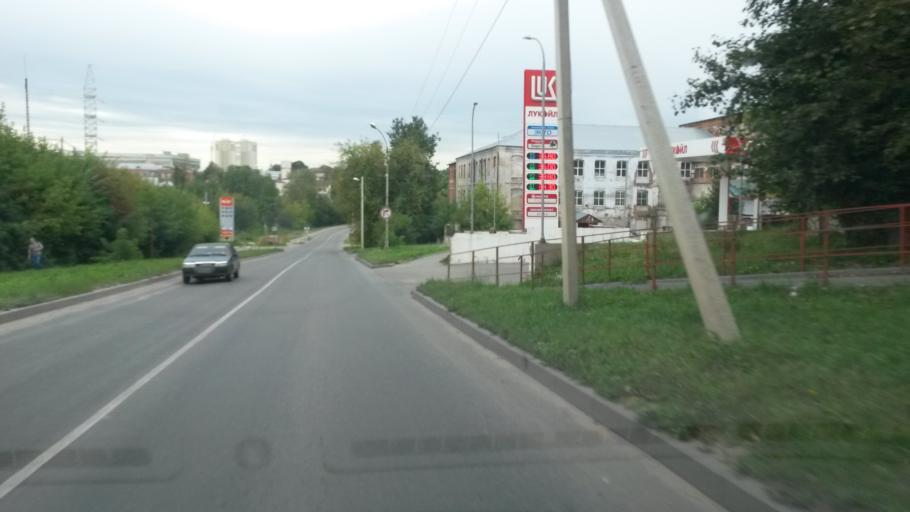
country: RU
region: Ivanovo
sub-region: Gorod Ivanovo
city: Ivanovo
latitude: 57.0158
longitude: 40.9563
